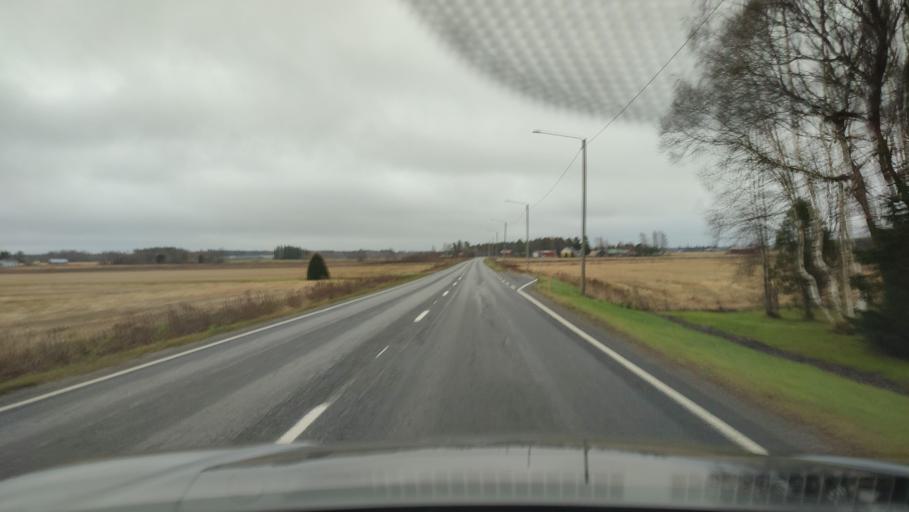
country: FI
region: Southern Ostrobothnia
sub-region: Suupohja
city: Isojoki
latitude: 62.1815
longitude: 21.8202
